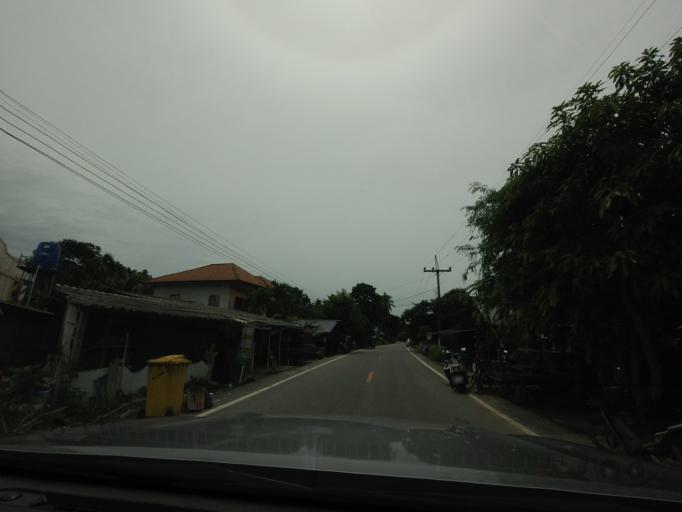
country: TH
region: Pattani
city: Kapho
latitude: 6.6072
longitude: 101.5366
